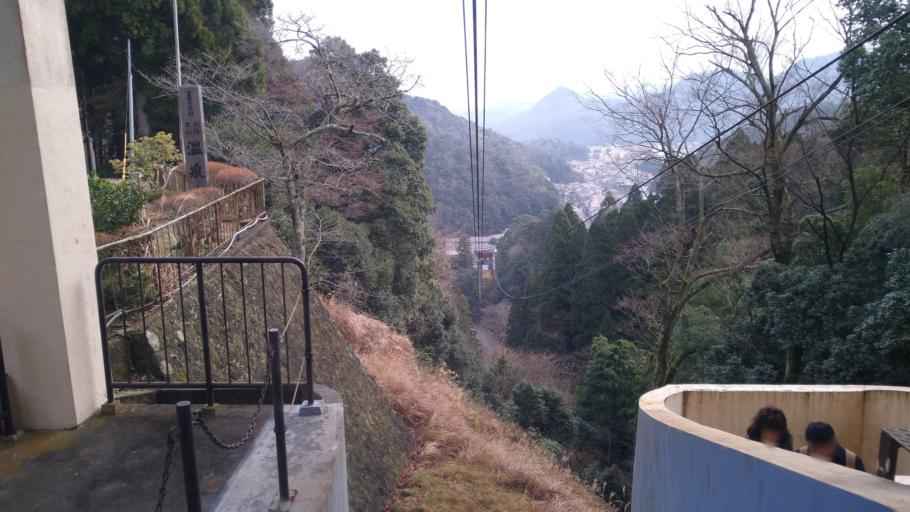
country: JP
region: Hyogo
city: Toyooka
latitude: 35.6240
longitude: 134.8005
